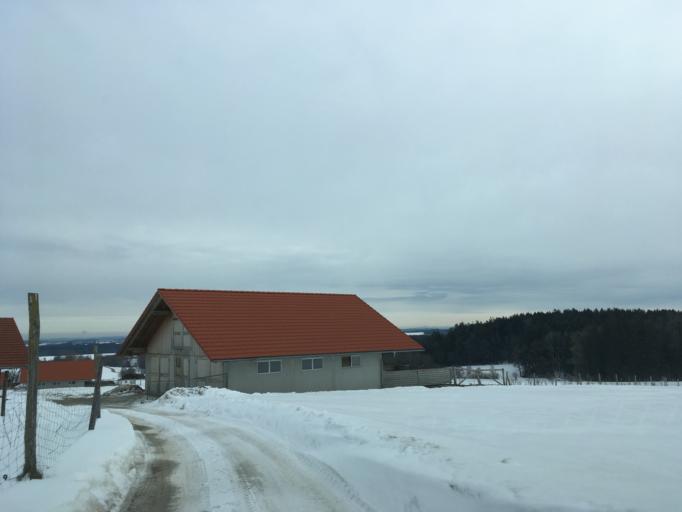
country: DE
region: Bavaria
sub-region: Upper Bavaria
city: Schnaitsee
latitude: 48.0823
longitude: 12.3783
